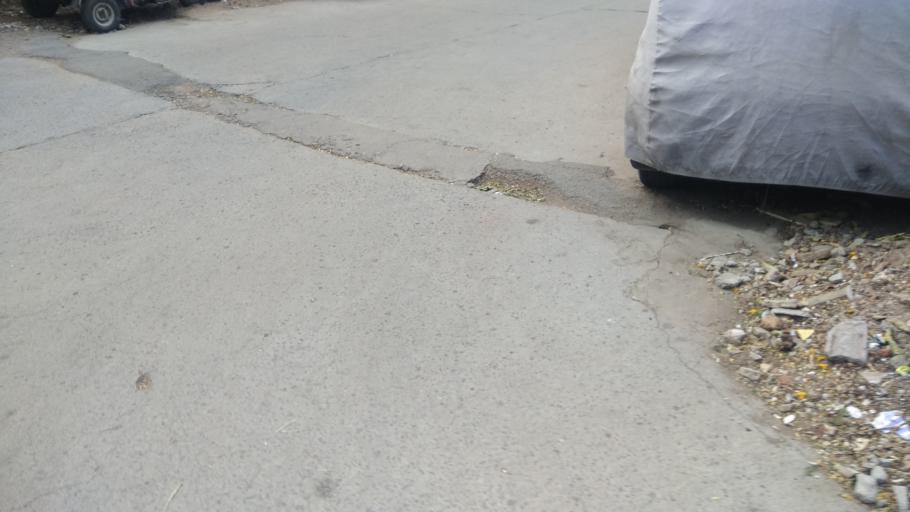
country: IN
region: Telangana
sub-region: Rangareddi
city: Kukatpalli
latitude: 17.4492
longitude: 78.4264
